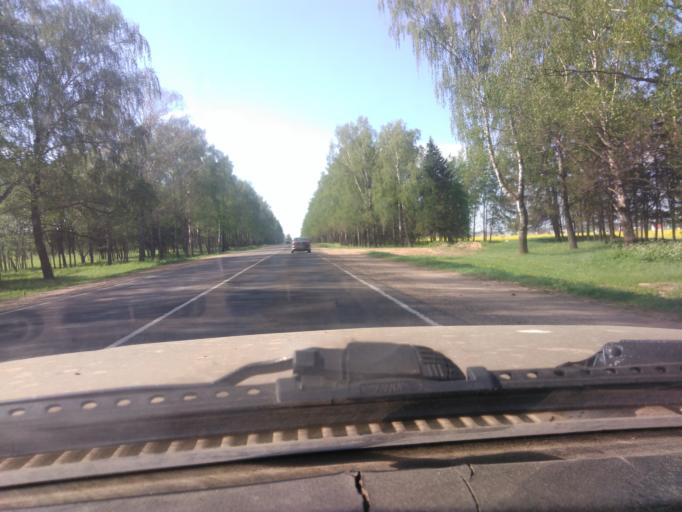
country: BY
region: Mogilev
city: Buynichy
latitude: 53.8470
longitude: 30.2513
